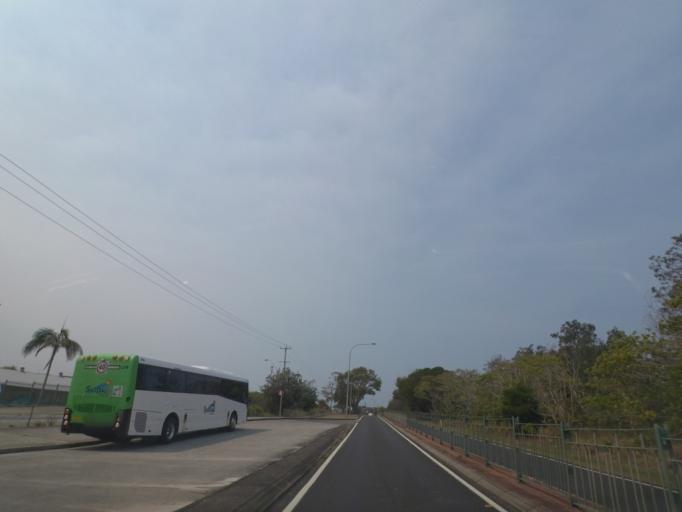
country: AU
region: New South Wales
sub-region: Tweed
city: Casuarina
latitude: -28.3386
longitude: 153.5730
